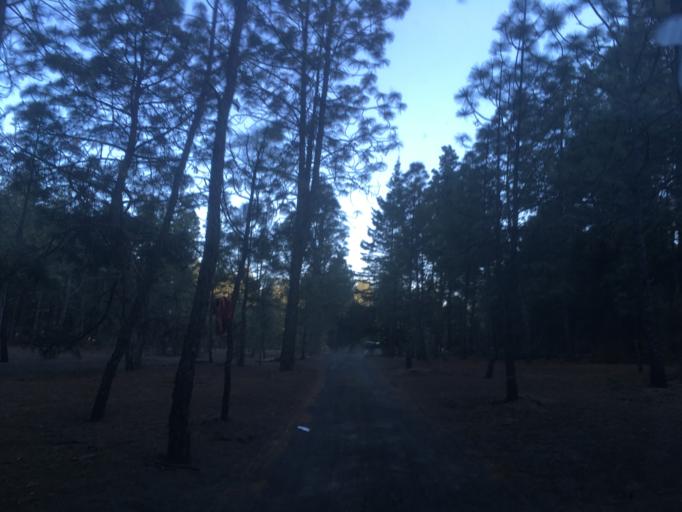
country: MX
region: Michoacan
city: Angahuan
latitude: 19.4674
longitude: -102.2401
